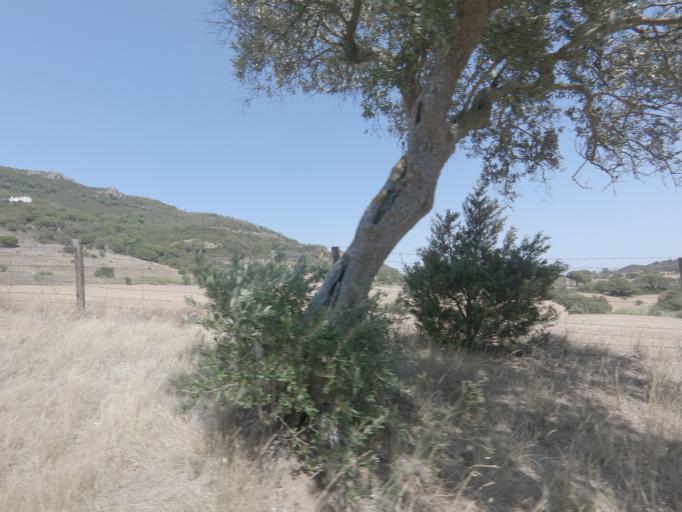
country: PT
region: Setubal
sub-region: Setubal
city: Setubal
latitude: 38.5244
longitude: -8.9324
